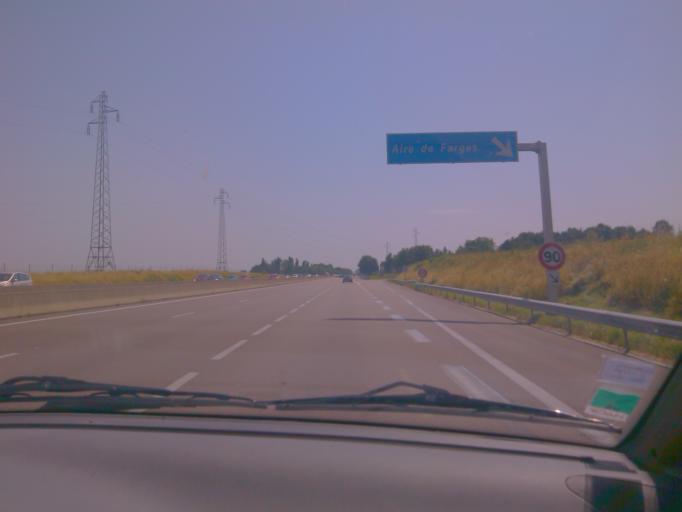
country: FR
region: Bourgogne
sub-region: Departement de Saone-et-Loire
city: Tournus
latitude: 46.5966
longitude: 4.8928
